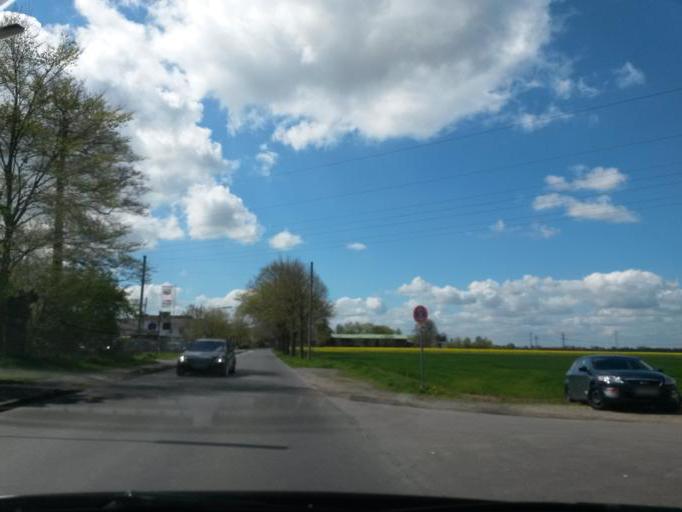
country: DE
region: Schleswig-Holstein
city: Uetersen
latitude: 53.6822
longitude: 9.6492
